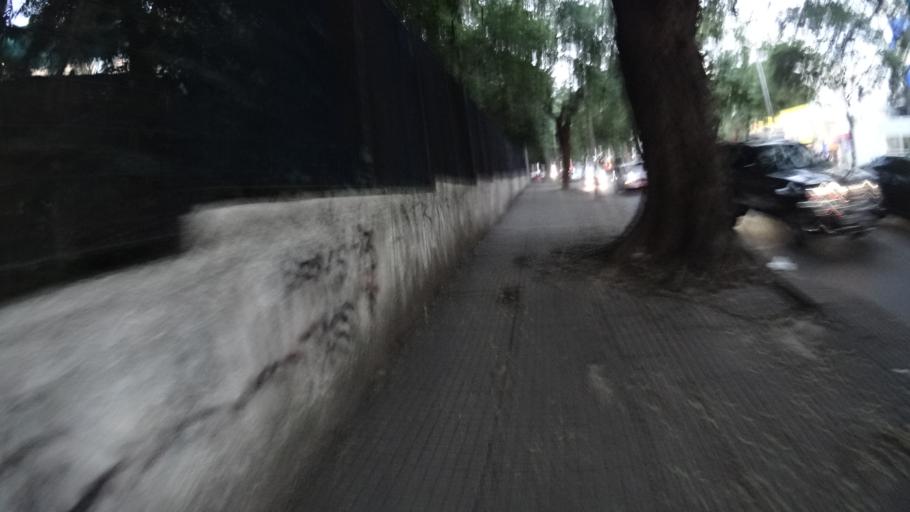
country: BR
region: Sao Paulo
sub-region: Sao Paulo
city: Sao Paulo
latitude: -23.5600
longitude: -46.6714
